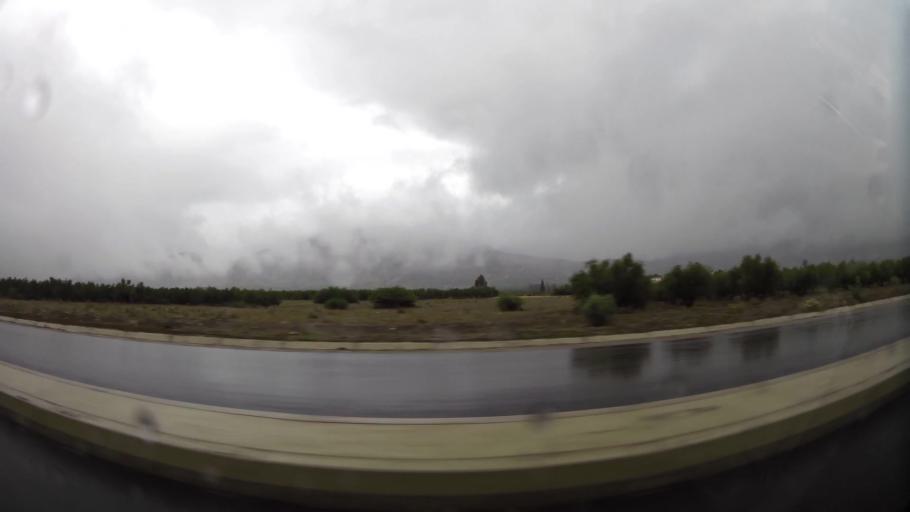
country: MA
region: Oriental
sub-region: Nador
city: Midar
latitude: 34.8341
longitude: -3.7200
